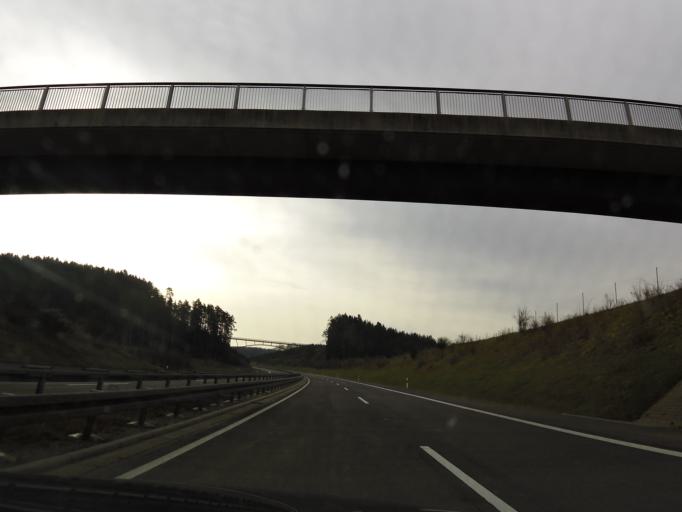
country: DE
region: Thuringia
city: Schleusingen
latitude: 50.4953
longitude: 10.7973
